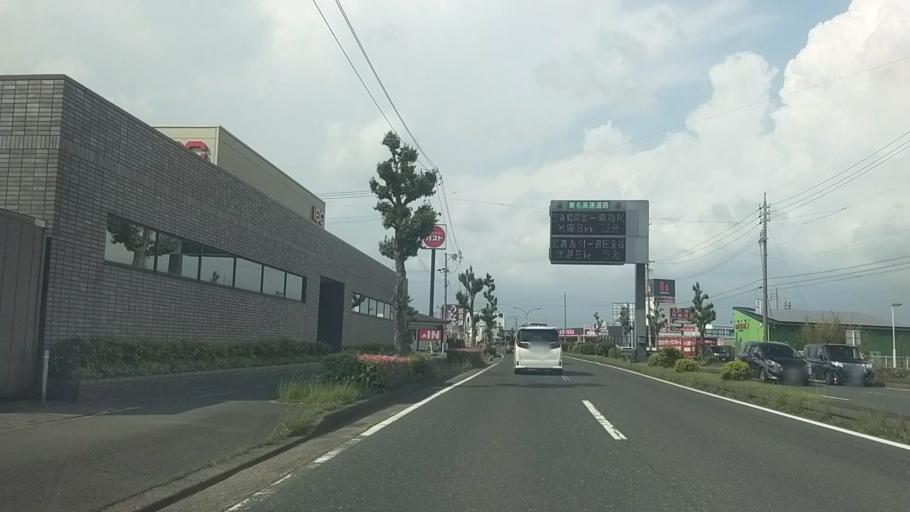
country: JP
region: Shizuoka
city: Hamakita
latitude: 34.7371
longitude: 137.7893
